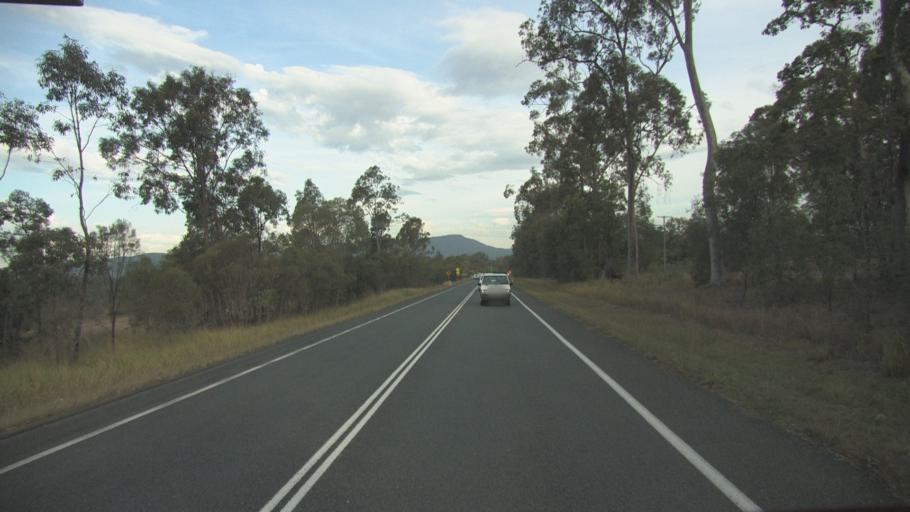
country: AU
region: Queensland
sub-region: Logan
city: Cedar Vale
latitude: -27.8463
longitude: 153.1197
